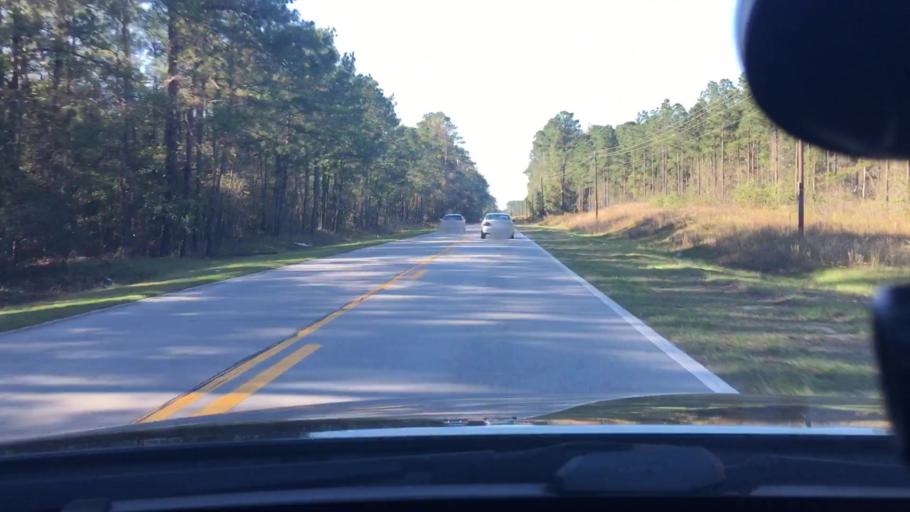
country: US
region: North Carolina
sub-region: Craven County
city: Vanceboro
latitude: 35.2193
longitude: -77.1231
